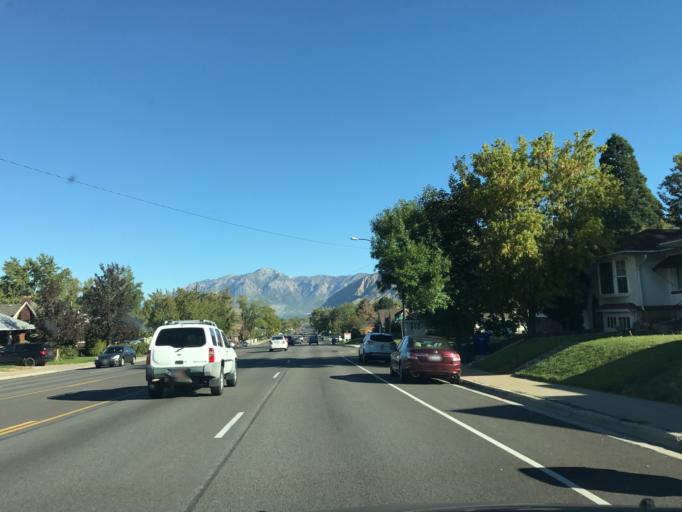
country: US
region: Utah
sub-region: Weber County
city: Ogden
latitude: 41.2146
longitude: -111.9483
